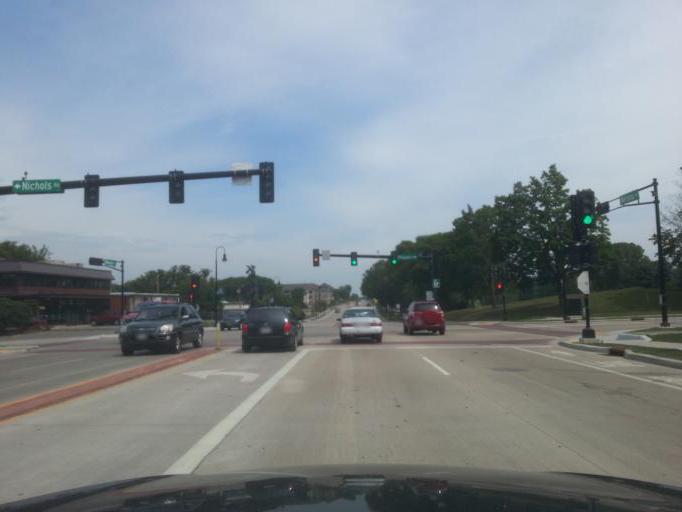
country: US
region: Wisconsin
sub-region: Dane County
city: Monona
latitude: 43.0620
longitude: -89.3261
